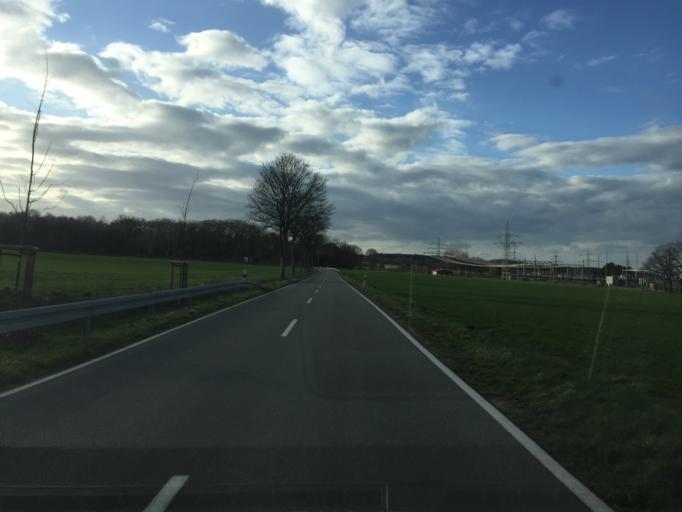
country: DE
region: Lower Saxony
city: Uchte
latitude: 52.5610
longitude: 8.8980
